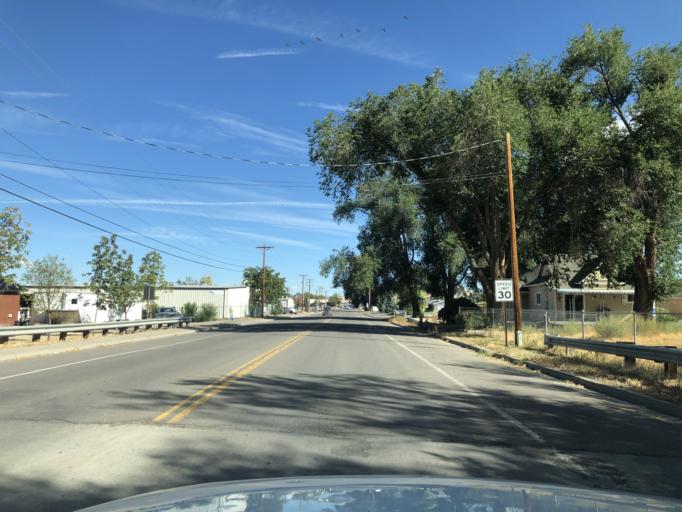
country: US
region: Colorado
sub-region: Montrose County
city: Montrose
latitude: 38.4848
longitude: -107.8571
